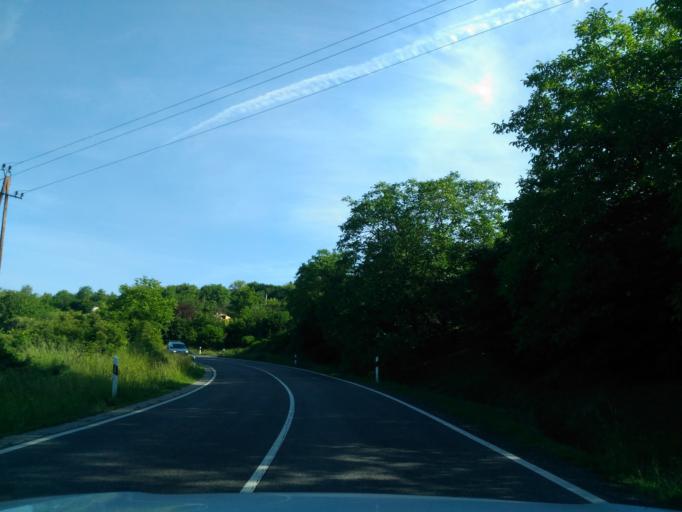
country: HU
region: Baranya
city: Komlo
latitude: 46.1725
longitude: 18.2630
